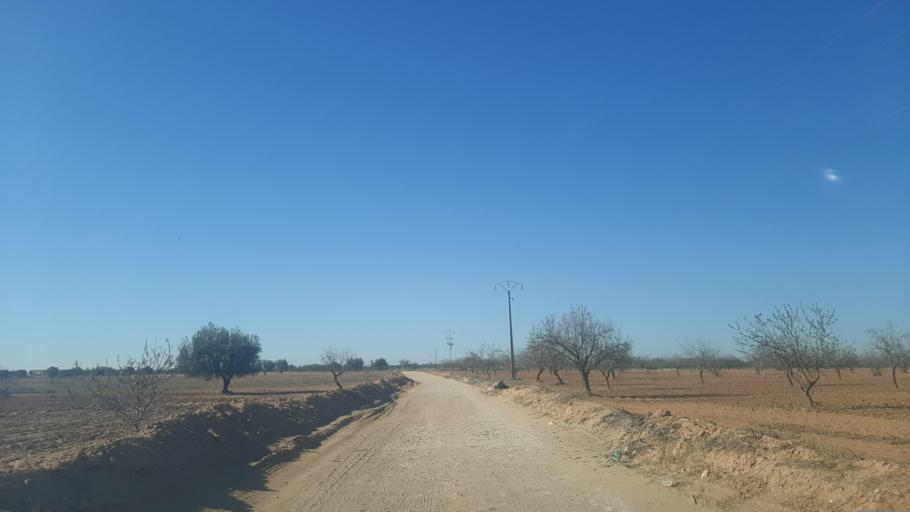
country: TN
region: Safaqis
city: Sfax
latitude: 34.8882
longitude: 10.5879
